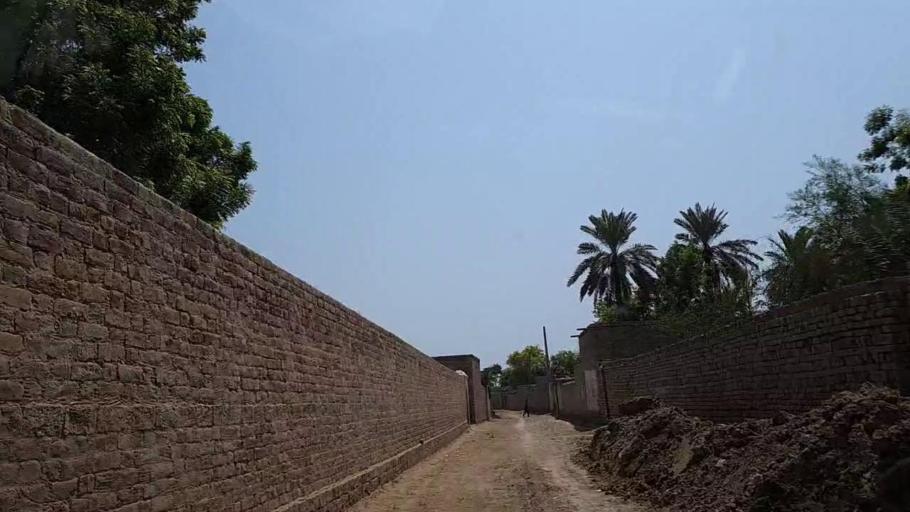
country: PK
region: Sindh
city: Adilpur
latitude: 27.9660
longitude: 69.3881
